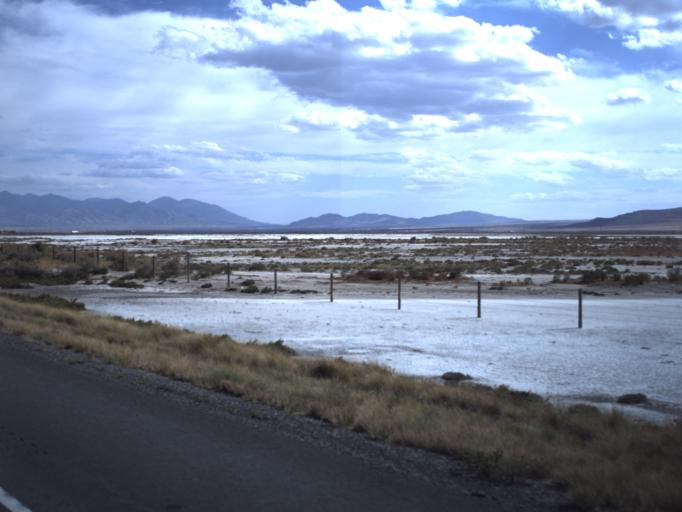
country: US
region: Utah
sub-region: Tooele County
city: Grantsville
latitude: 40.7157
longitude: -112.5449
